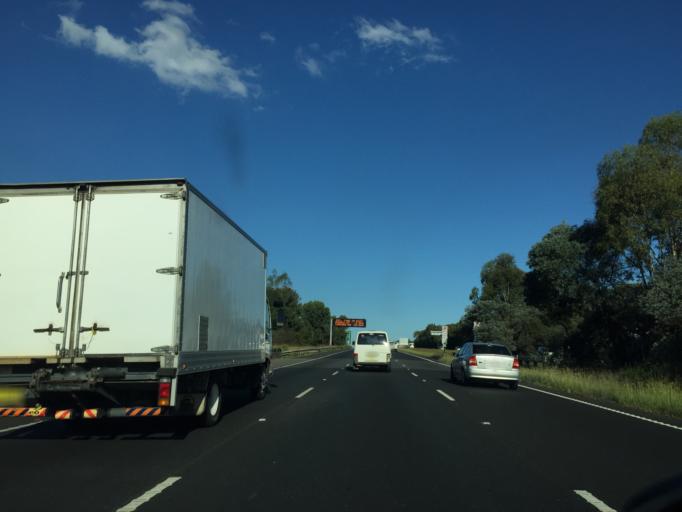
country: AU
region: New South Wales
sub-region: Blacktown
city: Doonside
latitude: -33.8008
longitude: 150.8694
